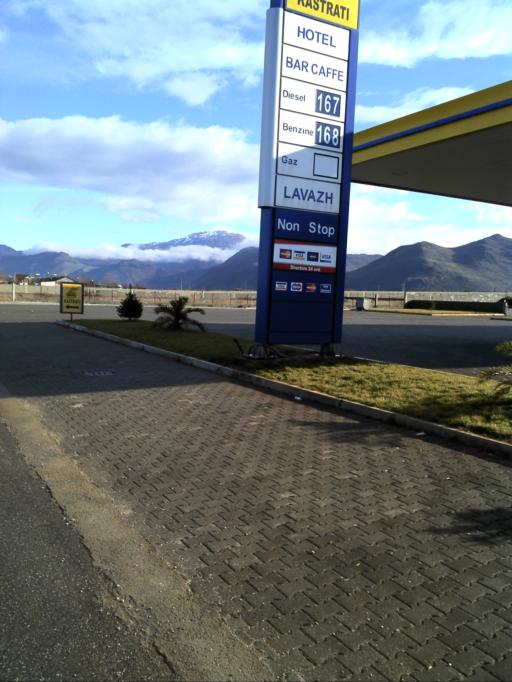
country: AL
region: Shkoder
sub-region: Rrethi i Malesia e Madhe
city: Koplik
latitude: 42.2532
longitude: 19.4268
